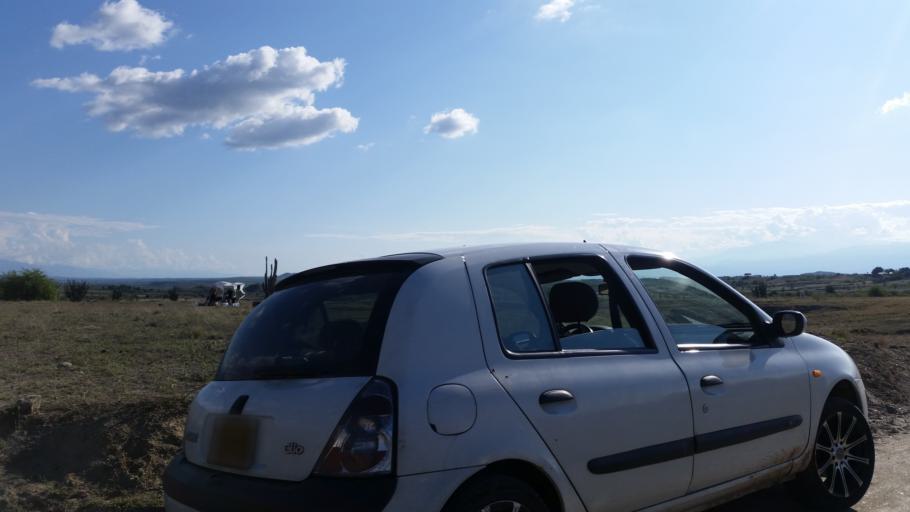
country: CO
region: Huila
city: Baraya
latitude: 3.2365
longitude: -75.1105
